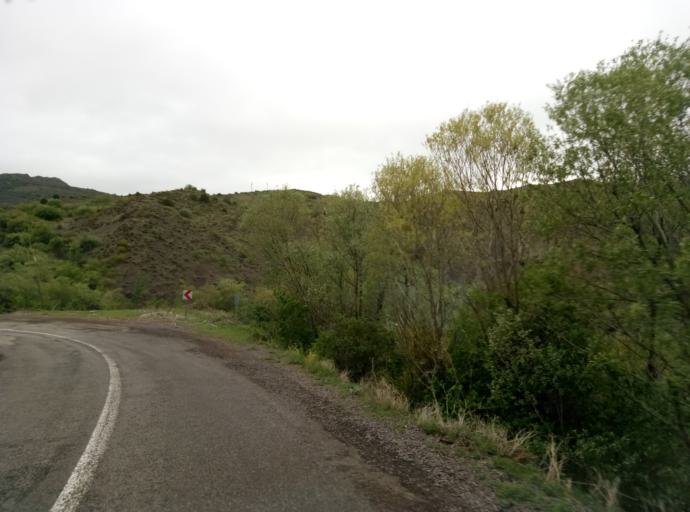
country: TR
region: Sivas
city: Koyulhisar
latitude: 40.1706
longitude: 37.8989
